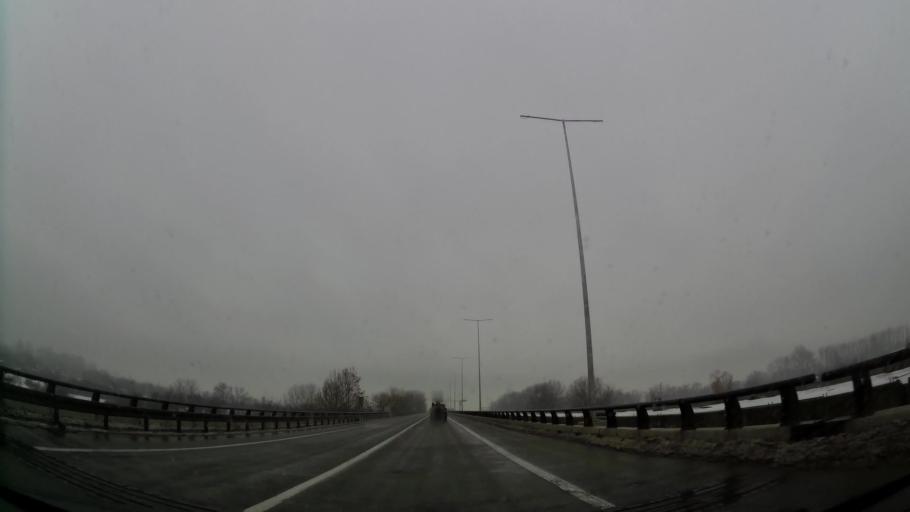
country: RS
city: Ostruznica
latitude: 44.7371
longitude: 20.3278
